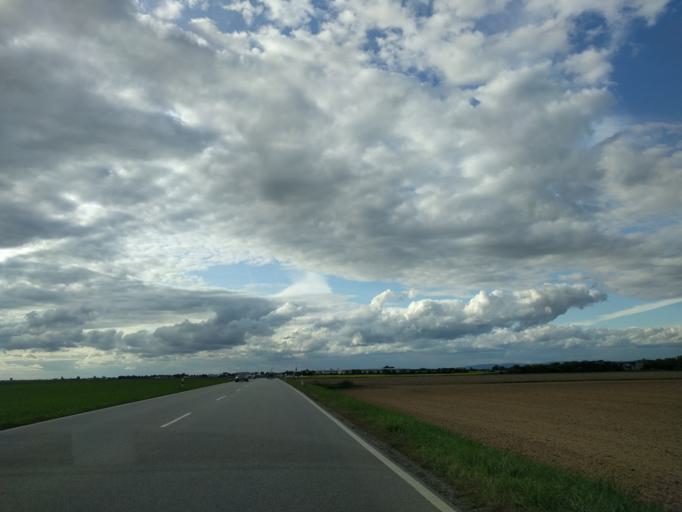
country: DE
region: Bavaria
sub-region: Lower Bavaria
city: Irlbach
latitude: 48.8193
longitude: 12.7512
